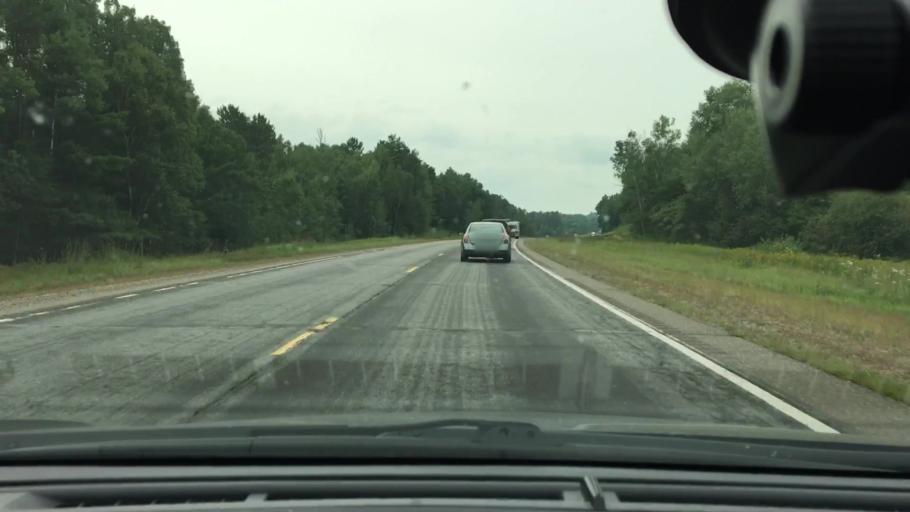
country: US
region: Minnesota
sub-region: Crow Wing County
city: Cross Lake
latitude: 46.6696
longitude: -93.9517
